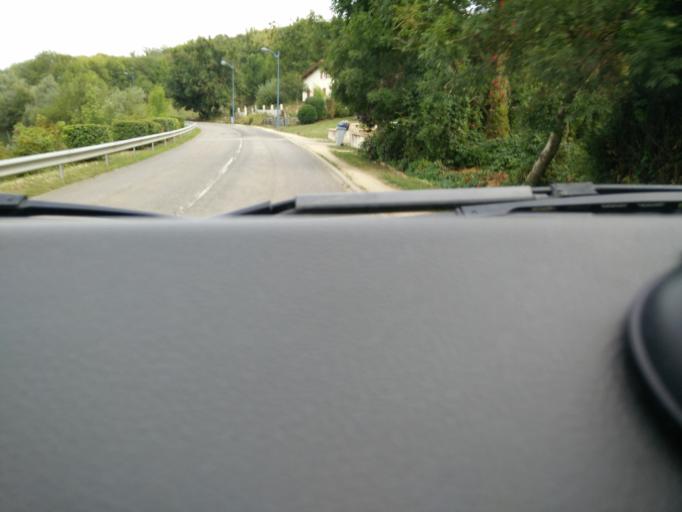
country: FR
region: Lorraine
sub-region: Departement de Meurthe-et-Moselle
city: Belleville
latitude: 48.8193
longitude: 6.1263
